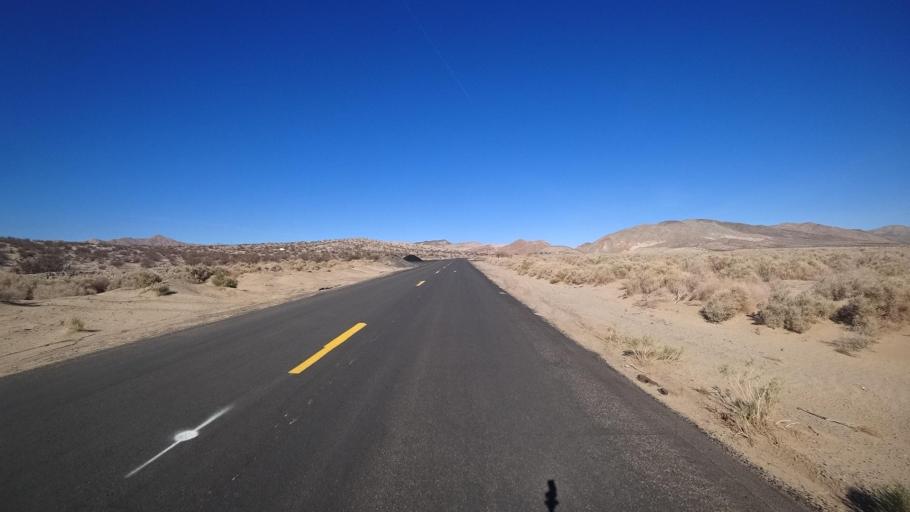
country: US
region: California
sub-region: Kern County
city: California City
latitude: 35.3224
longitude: -117.9627
